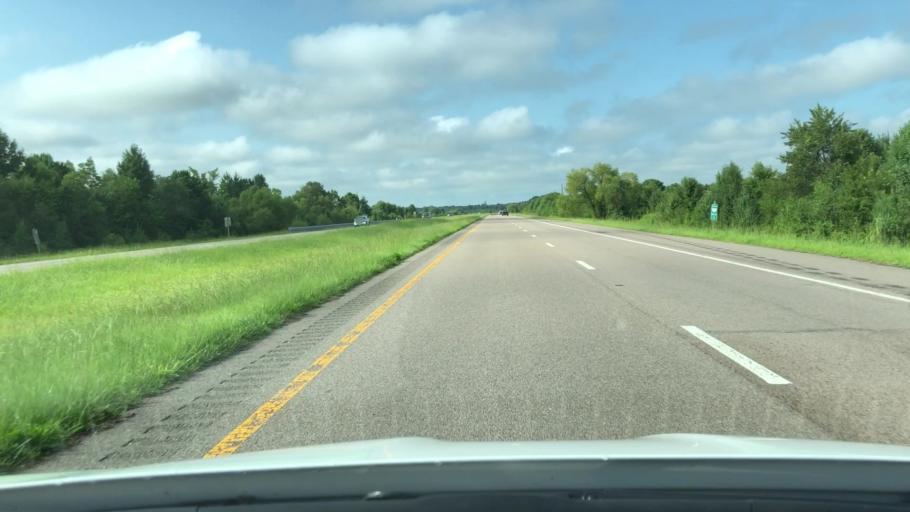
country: US
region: Virginia
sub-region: City of Portsmouth
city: Portsmouth Heights
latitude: 36.6991
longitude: -76.3445
